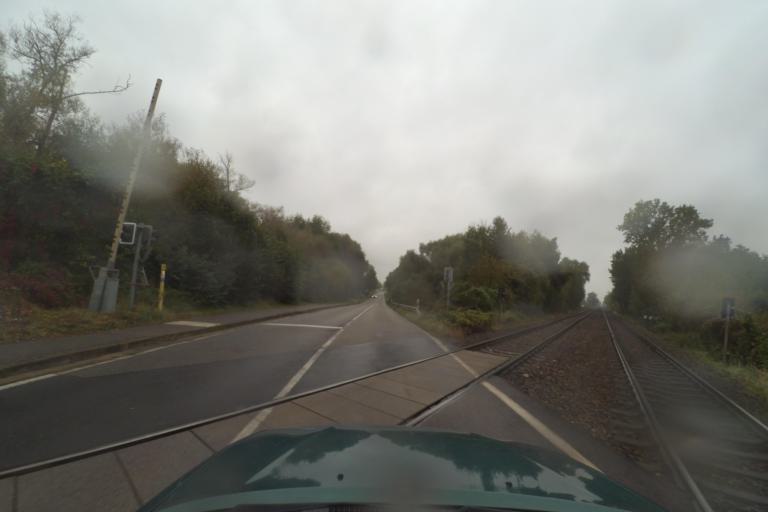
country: DE
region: Rheinland-Pfalz
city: Steinweiler
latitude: 49.1293
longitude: 8.1359
